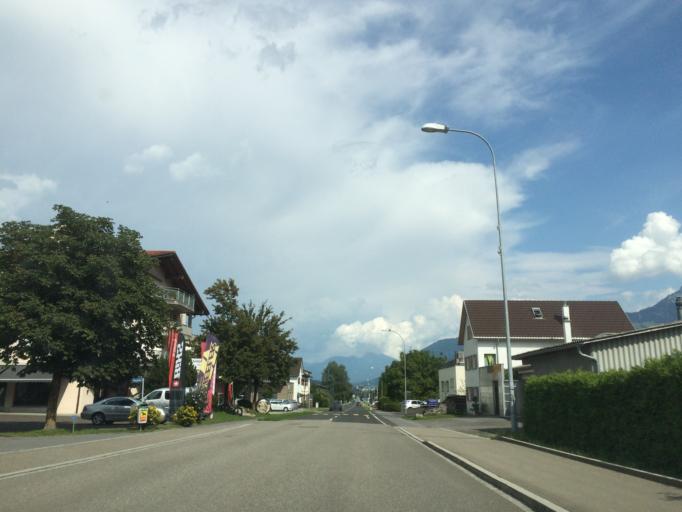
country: CH
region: Saint Gallen
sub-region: Wahlkreis Werdenberg
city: Gams
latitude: 47.2049
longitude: 9.4490
